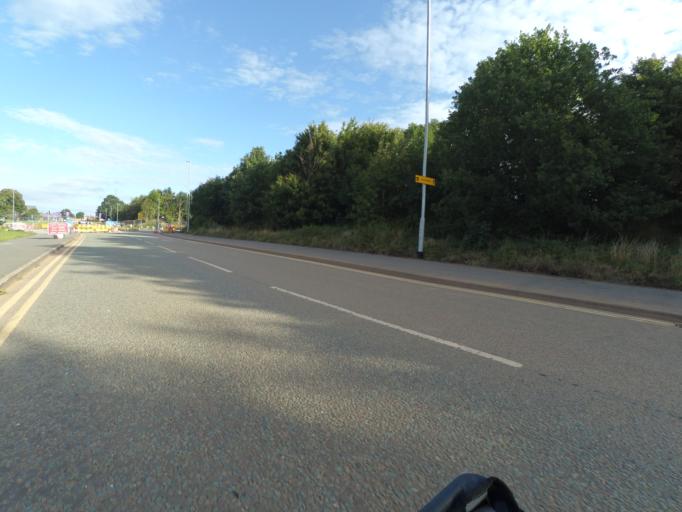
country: GB
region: England
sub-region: Staffordshire
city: Stafford
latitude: 52.8059
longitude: -2.1322
